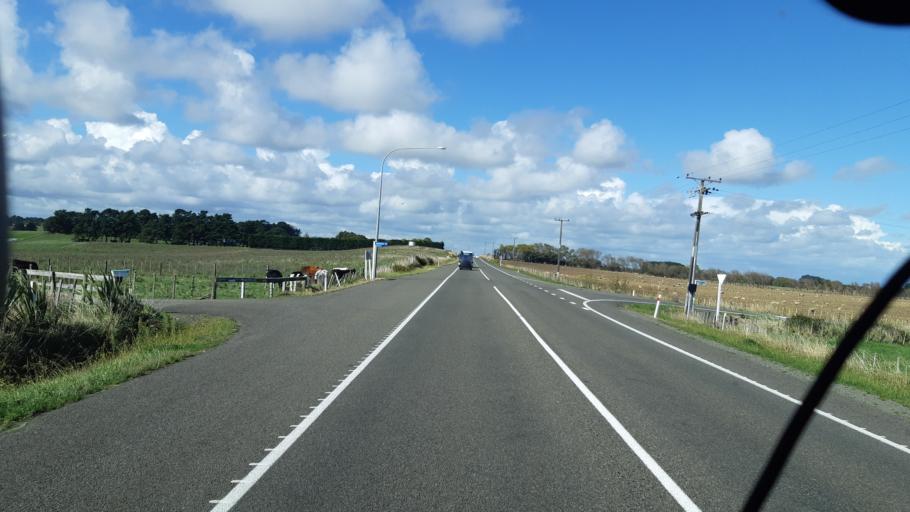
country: NZ
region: Manawatu-Wanganui
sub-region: Wanganui District
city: Wanganui
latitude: -39.9764
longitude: 175.1316
